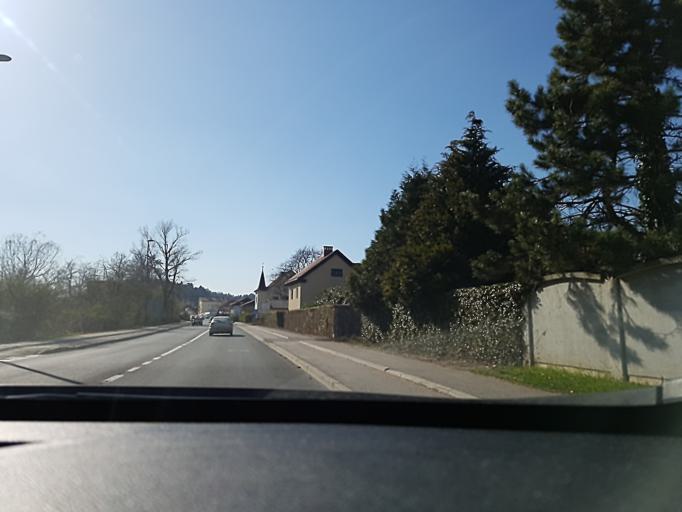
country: SI
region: Trzin
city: Trzin
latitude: 46.1048
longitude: 14.5409
